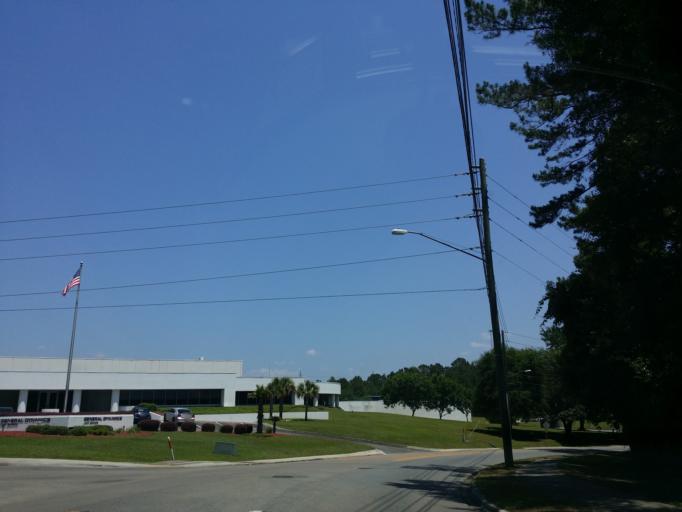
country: US
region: Florida
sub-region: Leon County
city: Tallahassee
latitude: 30.4731
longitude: -84.3488
